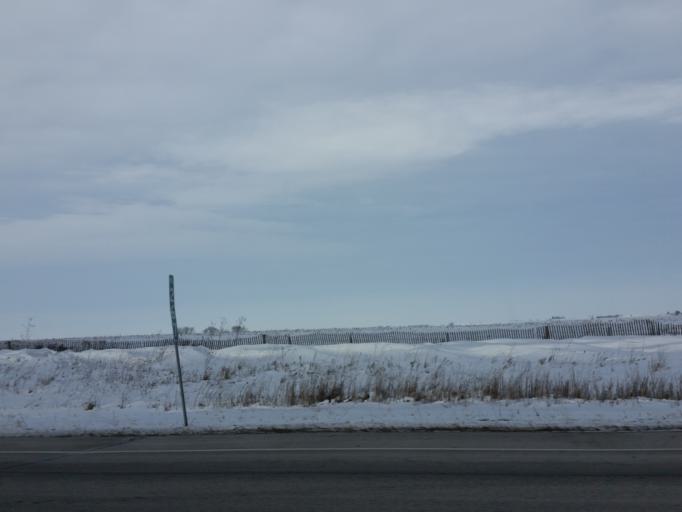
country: US
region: Iowa
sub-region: Delaware County
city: Manchester
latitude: 42.4641
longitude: -91.6409
